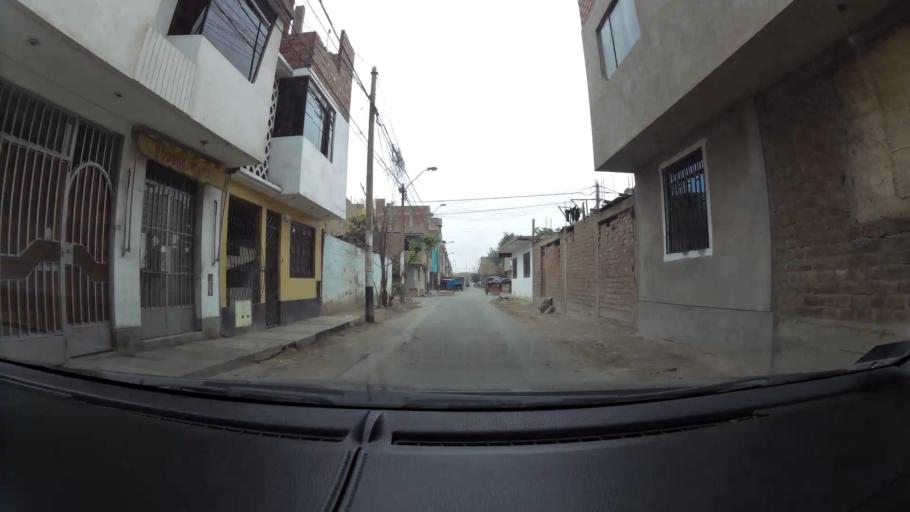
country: PE
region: Lima
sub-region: Lima
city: Independencia
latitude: -11.9587
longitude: -77.0823
